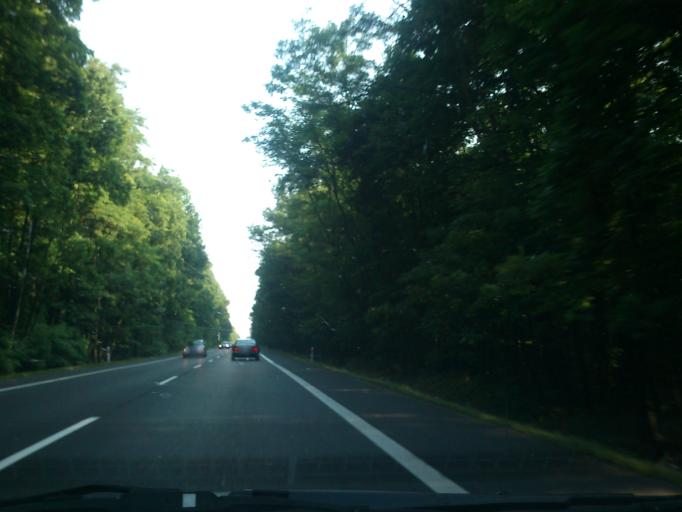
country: PL
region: Lower Silesian Voivodeship
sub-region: Legnica
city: Legnica
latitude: 51.2976
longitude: 16.1580
